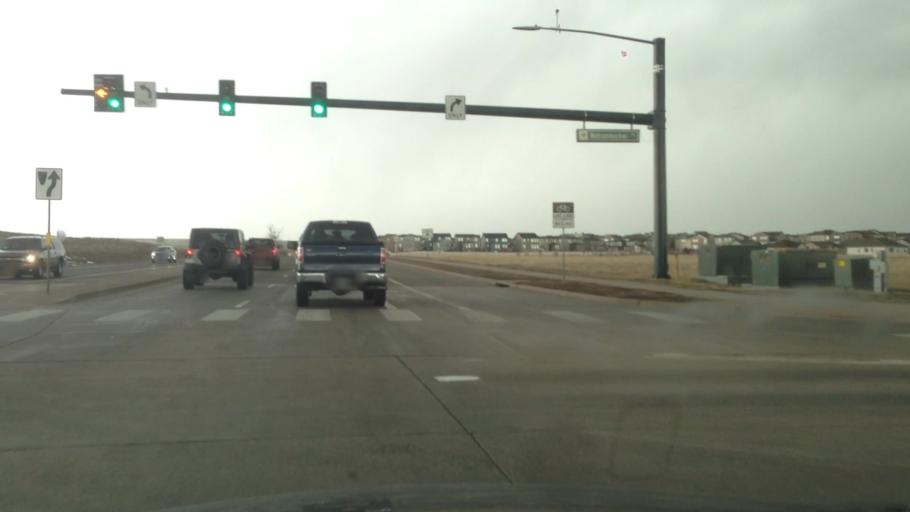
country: US
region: Colorado
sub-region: Douglas County
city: Parker
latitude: 39.4931
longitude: -104.7748
